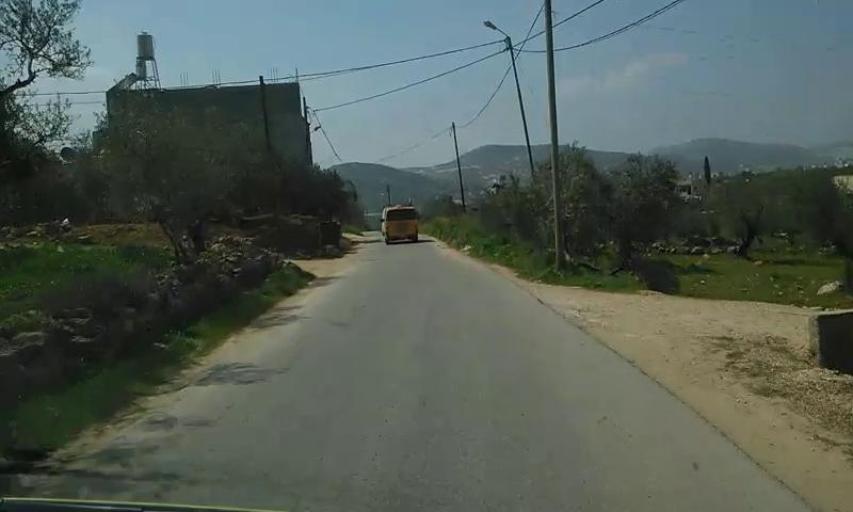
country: PS
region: West Bank
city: Udalah
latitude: 32.1429
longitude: 35.2723
